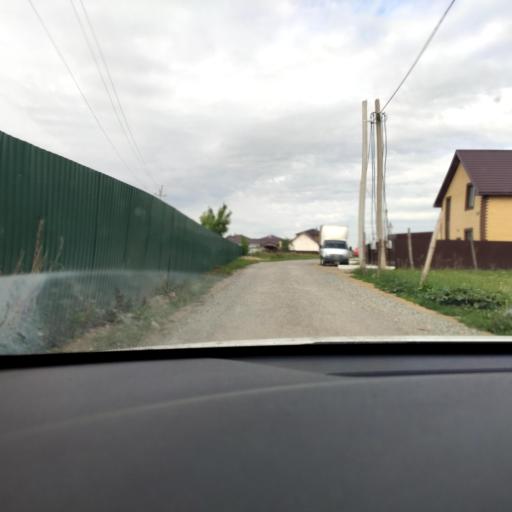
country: RU
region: Tatarstan
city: Stolbishchi
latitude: 55.6441
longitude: 49.3106
